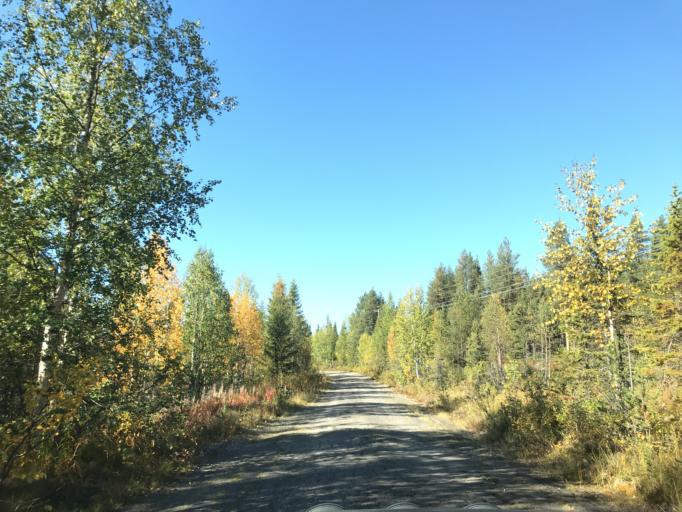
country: SE
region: Norrbotten
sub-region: Gallivare Kommun
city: Malmberget
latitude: 67.6470
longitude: 21.0878
